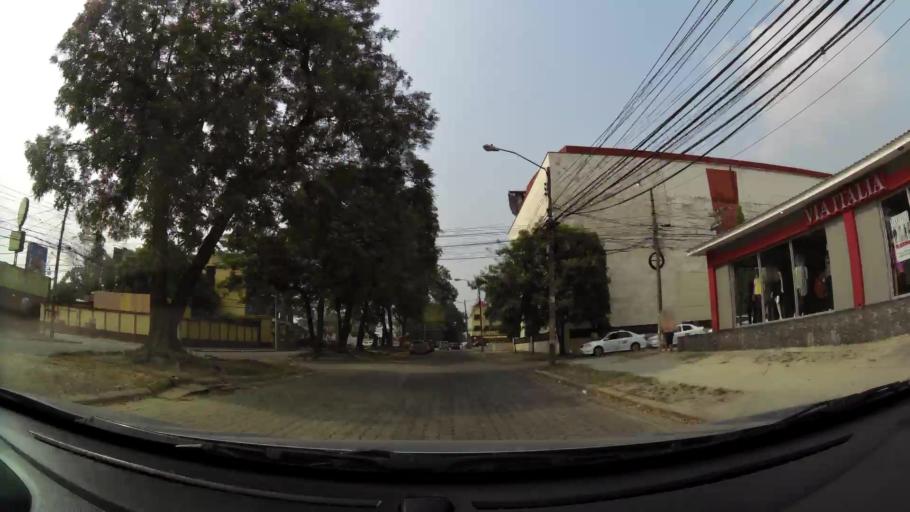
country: HN
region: Cortes
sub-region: San Pedro Sula
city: Pena Blanca
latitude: 15.5311
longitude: -88.0277
